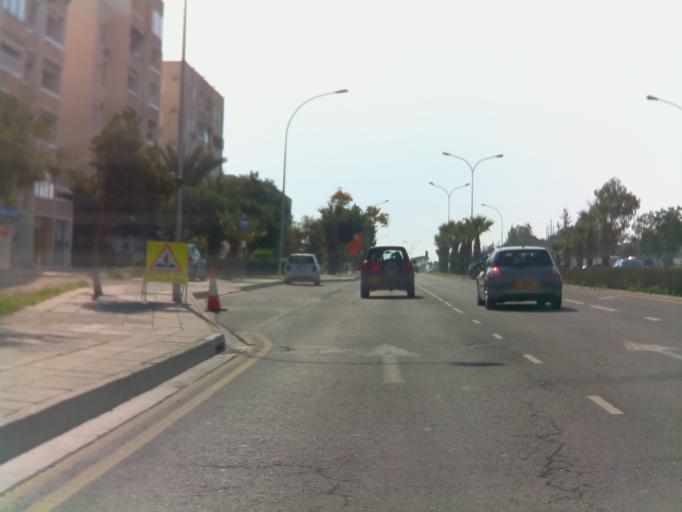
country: CY
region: Larnaka
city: Larnaca
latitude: 34.9026
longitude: 33.6304
